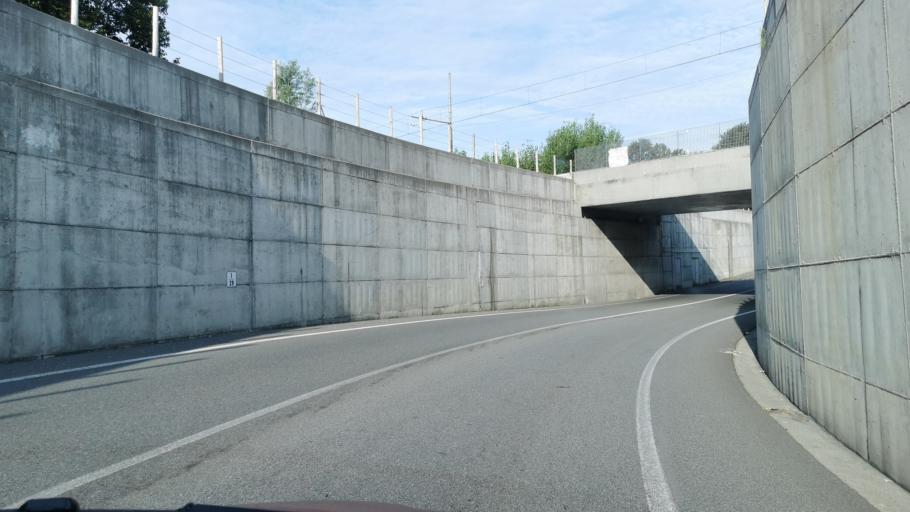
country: IT
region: Lombardy
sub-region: Provincia di Sondrio
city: Dubino
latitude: 46.1563
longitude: 9.4170
